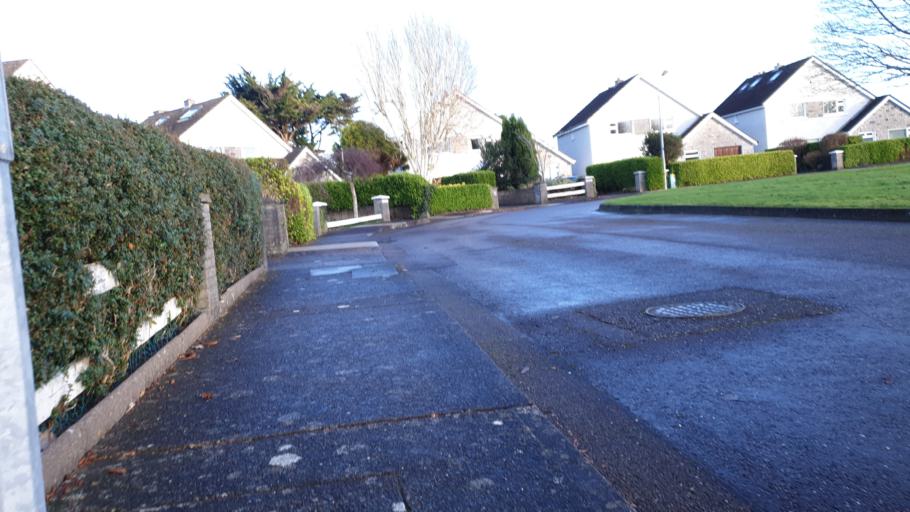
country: IE
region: Munster
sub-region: County Cork
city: Cork
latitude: 51.8936
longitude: -8.4256
